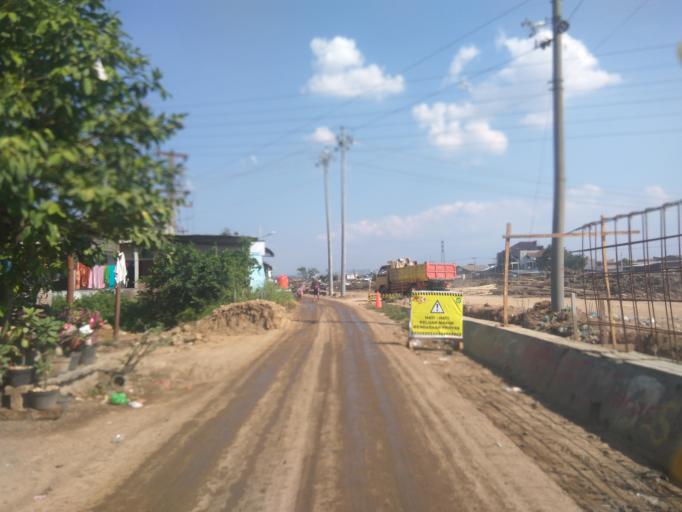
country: ID
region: Central Java
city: Semarang
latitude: -6.9525
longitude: 110.4407
